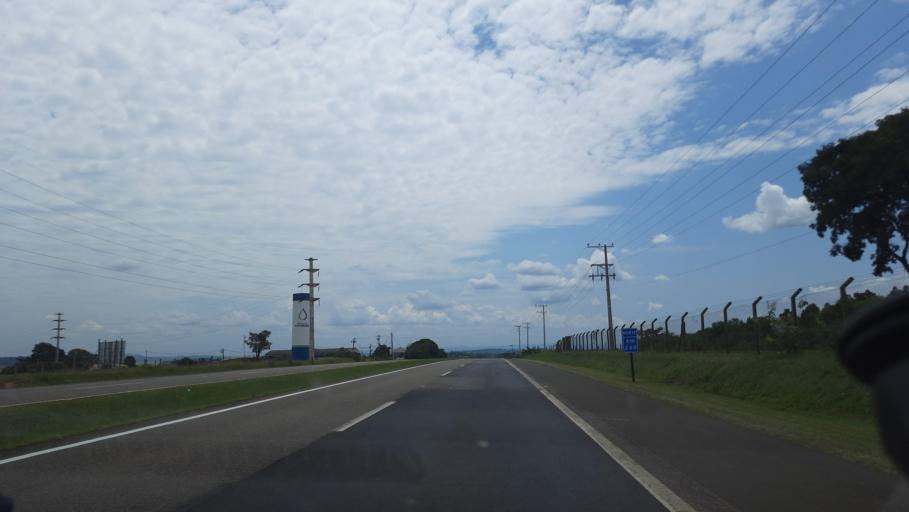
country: BR
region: Sao Paulo
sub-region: Casa Branca
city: Casa Branca
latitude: -21.7590
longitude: -47.0704
